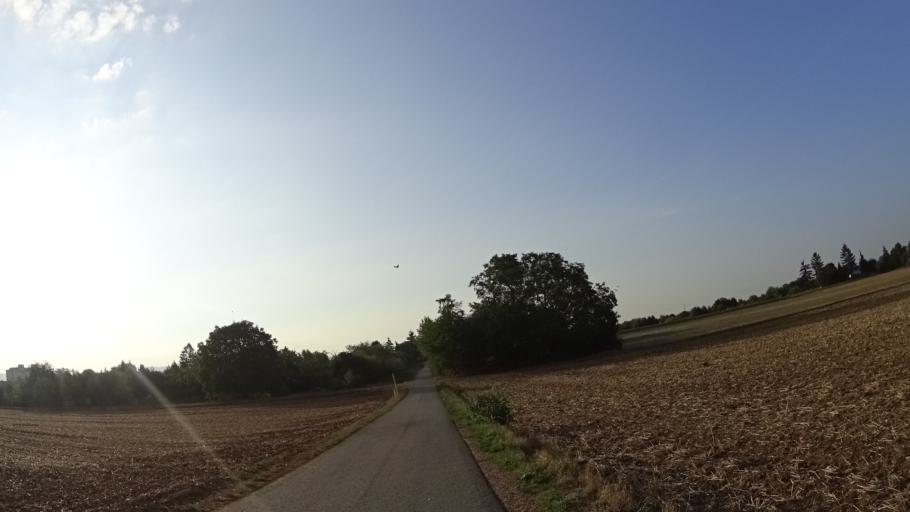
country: DE
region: Baden-Wuerttemberg
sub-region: Karlsruhe Region
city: Edingen-Neckarhausen
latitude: 49.4476
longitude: 8.5969
